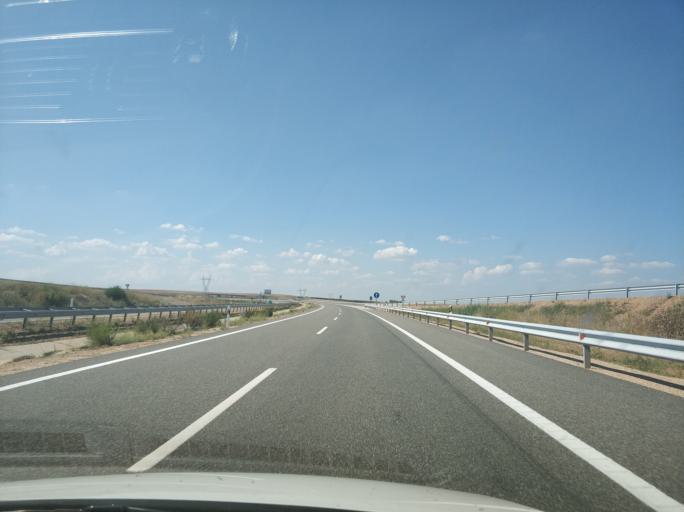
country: ES
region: Castille and Leon
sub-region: Provincia de Zamora
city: Manganeses de la Lampreana
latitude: 41.7636
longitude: -5.7557
